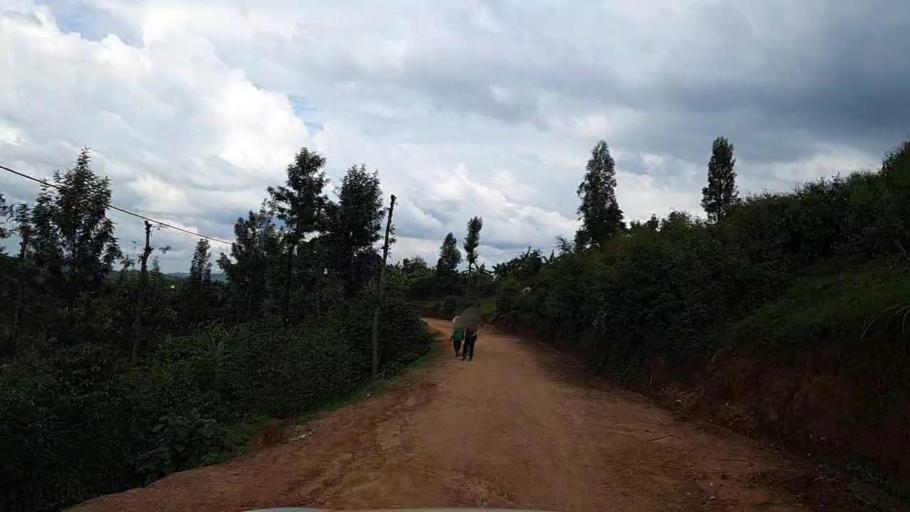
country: RW
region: Southern Province
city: Gikongoro
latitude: -2.4224
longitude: 29.6481
